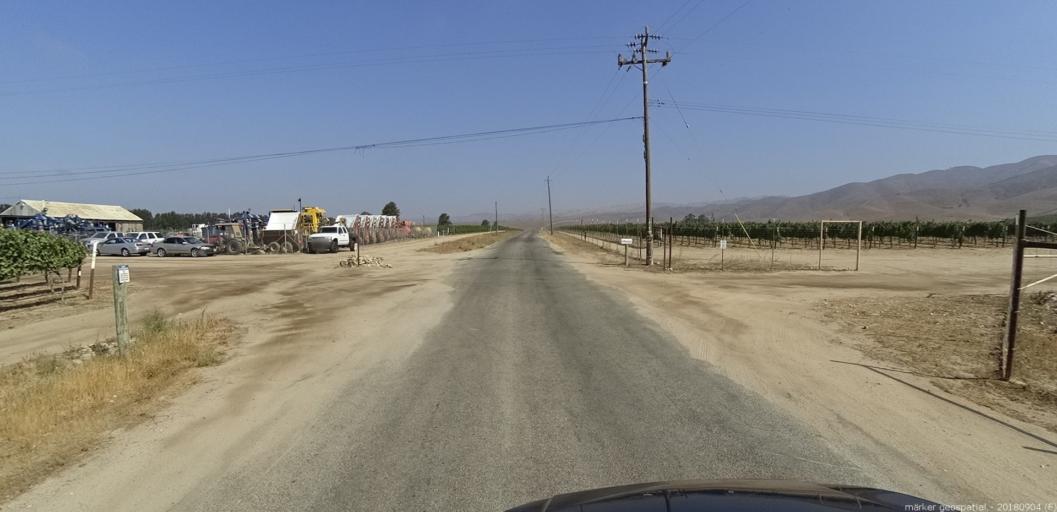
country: US
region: California
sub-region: Monterey County
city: Soledad
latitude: 36.4740
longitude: -121.3496
